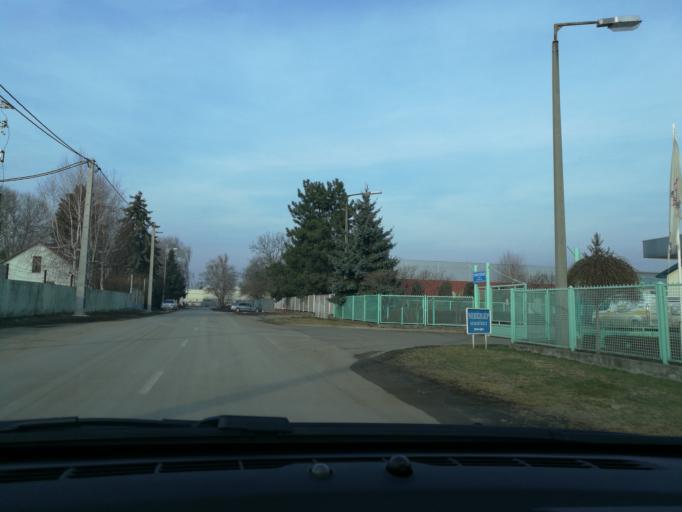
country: HU
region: Szabolcs-Szatmar-Bereg
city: Nyiregyhaza
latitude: 47.9399
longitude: 21.6916
